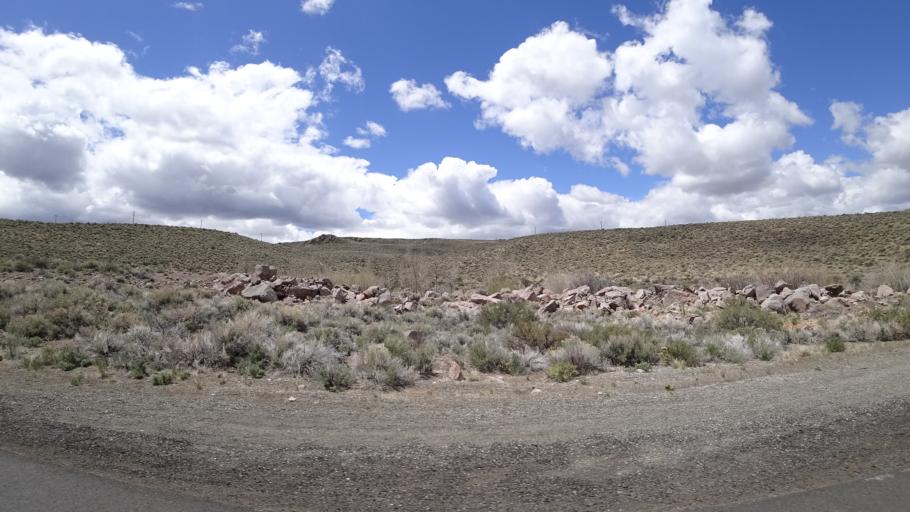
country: US
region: California
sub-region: Mono County
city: Bridgeport
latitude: 38.1788
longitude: -119.1960
